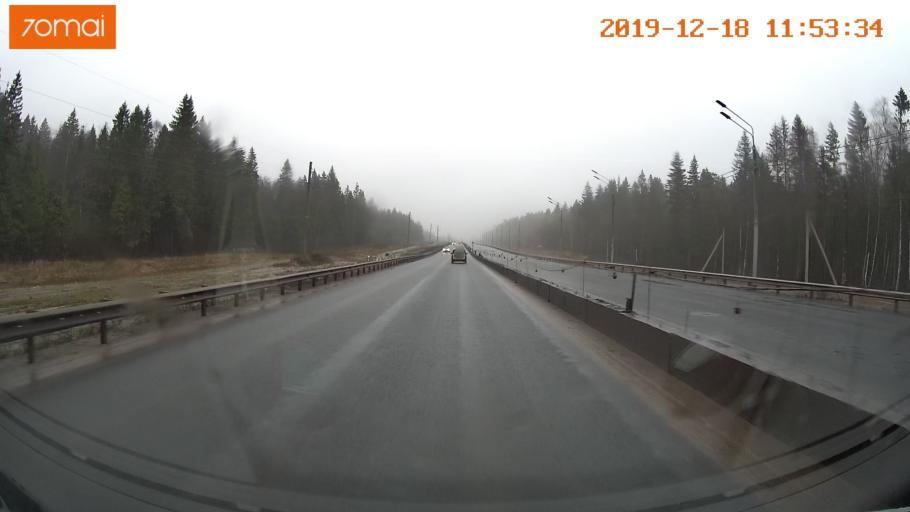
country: RU
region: Moskovskaya
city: Yershovo
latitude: 55.8059
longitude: 36.9197
